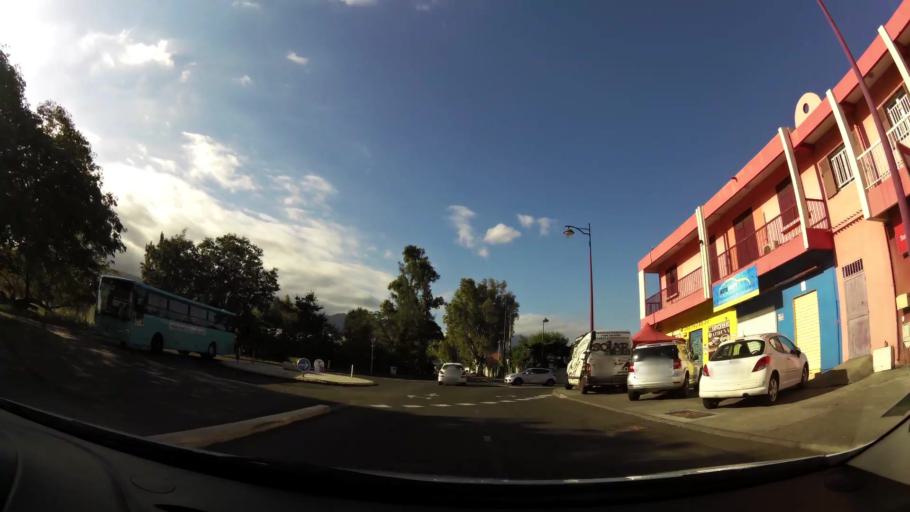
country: RE
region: Reunion
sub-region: Reunion
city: Saint-Louis
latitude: -21.2822
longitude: 55.4021
